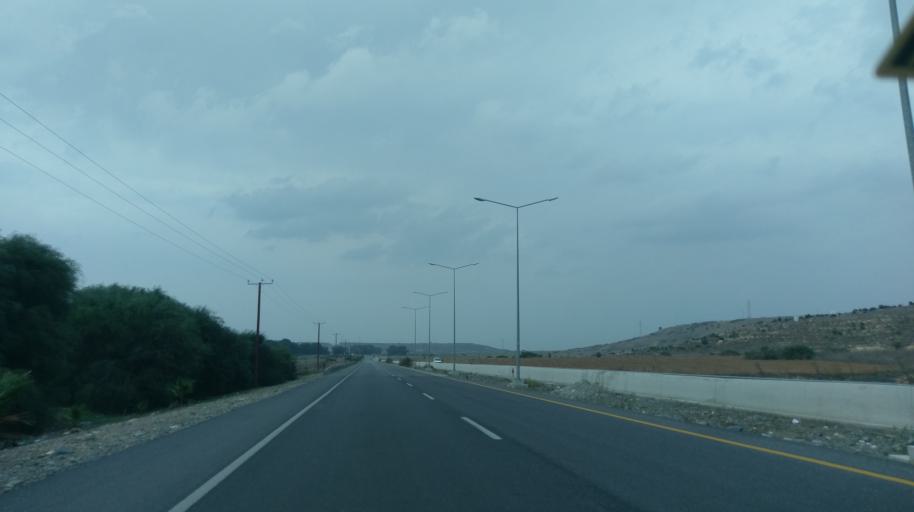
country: CY
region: Lefkosia
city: Akaki
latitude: 35.1953
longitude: 33.1062
